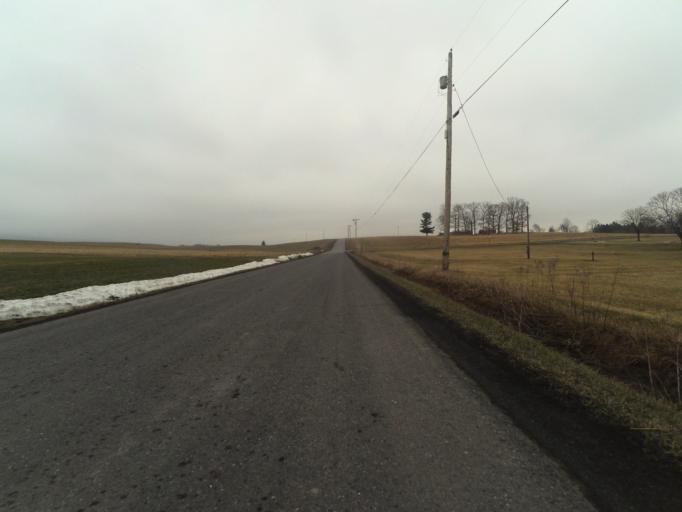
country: US
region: Pennsylvania
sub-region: Centre County
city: Centre Hall
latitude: 40.8490
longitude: -77.6571
